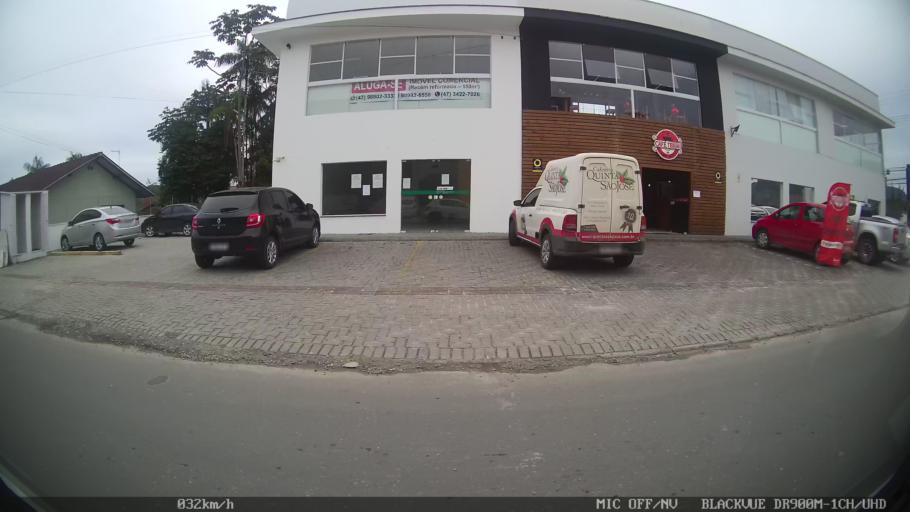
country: BR
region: Santa Catarina
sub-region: Joinville
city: Joinville
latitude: -26.2873
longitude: -48.9099
